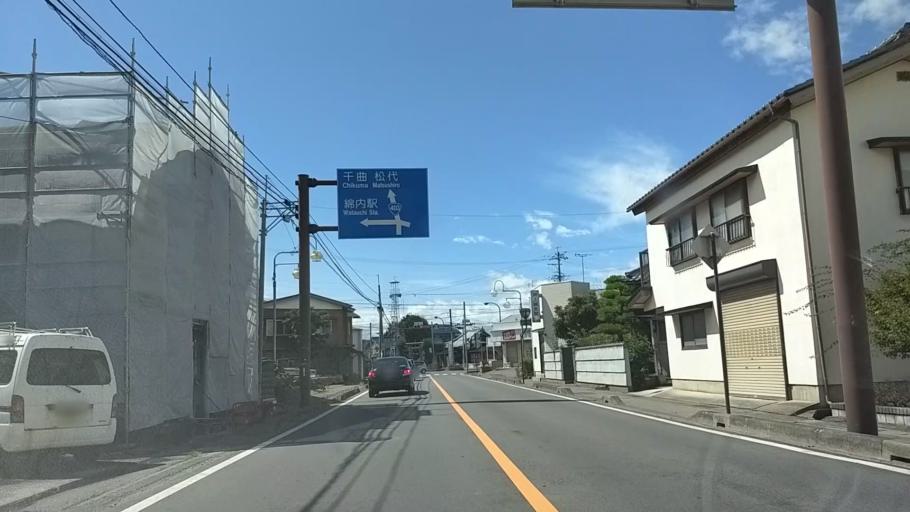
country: JP
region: Nagano
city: Suzaka
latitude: 36.6262
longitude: 138.2590
